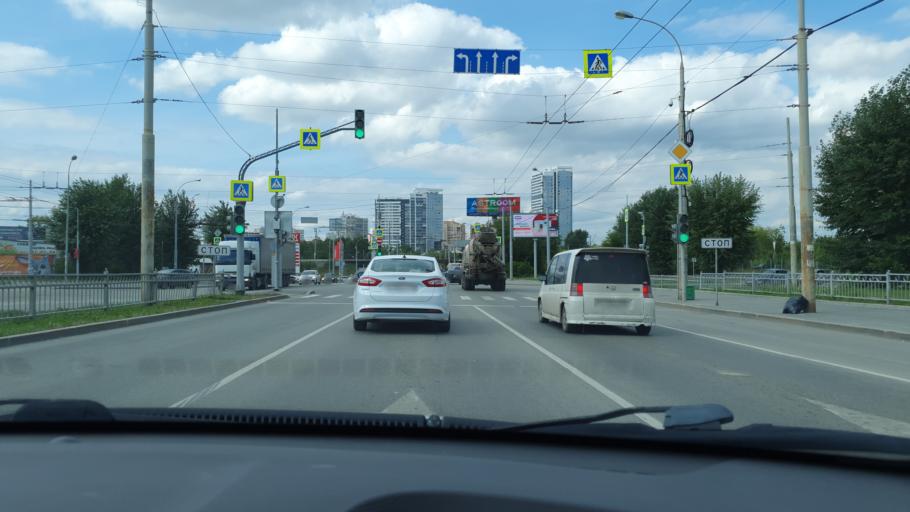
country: RU
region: Sverdlovsk
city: Yekaterinburg
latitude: 56.7919
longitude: 60.6437
